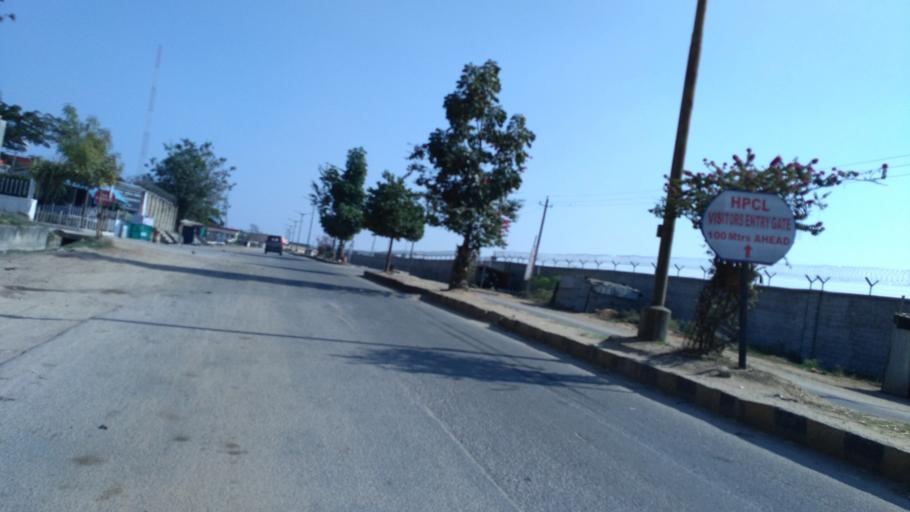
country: IN
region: Karnataka
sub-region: Hassan
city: Hassan
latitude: 12.9841
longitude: 76.1183
